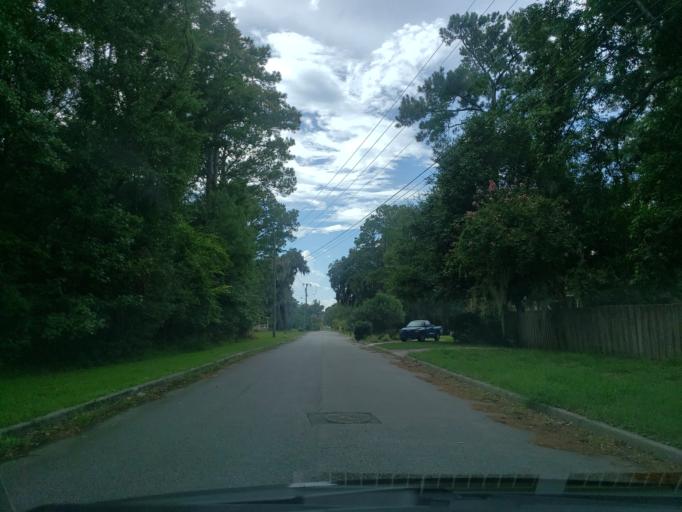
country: US
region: Georgia
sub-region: Chatham County
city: Isle of Hope
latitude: 31.9840
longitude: -81.0657
